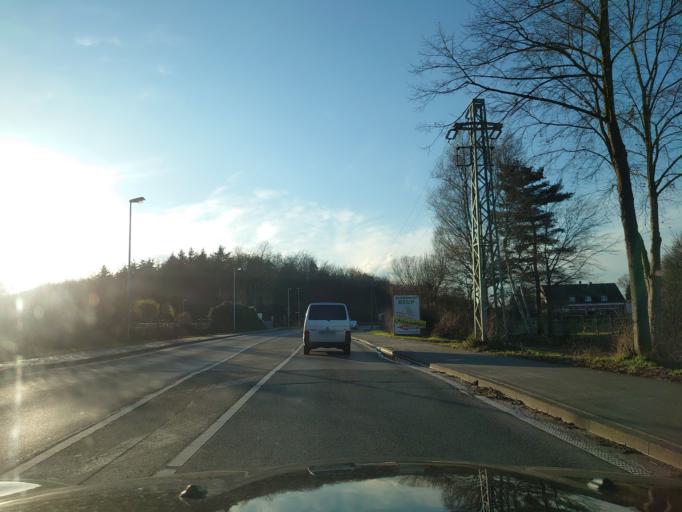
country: DE
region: North Rhine-Westphalia
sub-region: Regierungsbezirk Dusseldorf
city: Dormagen
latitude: 51.0782
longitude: 6.7725
